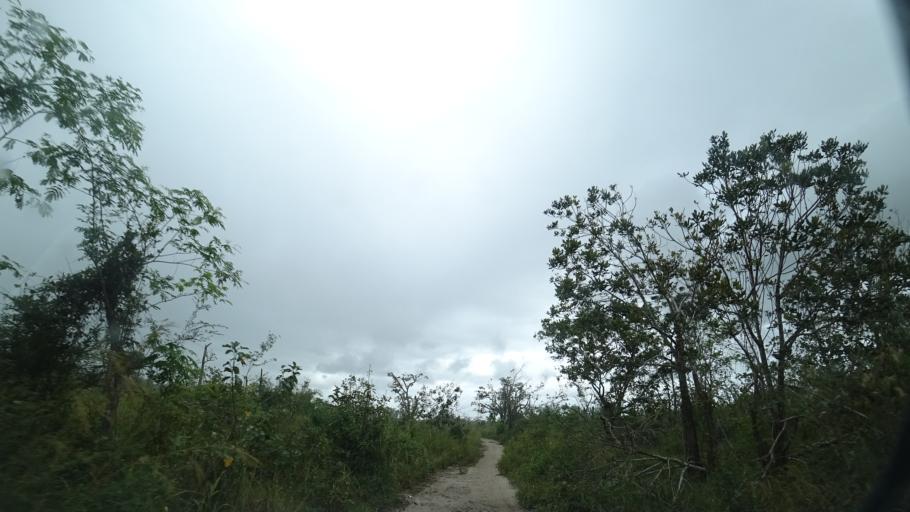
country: MZ
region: Sofala
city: Dondo
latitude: -19.5528
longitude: 35.0620
